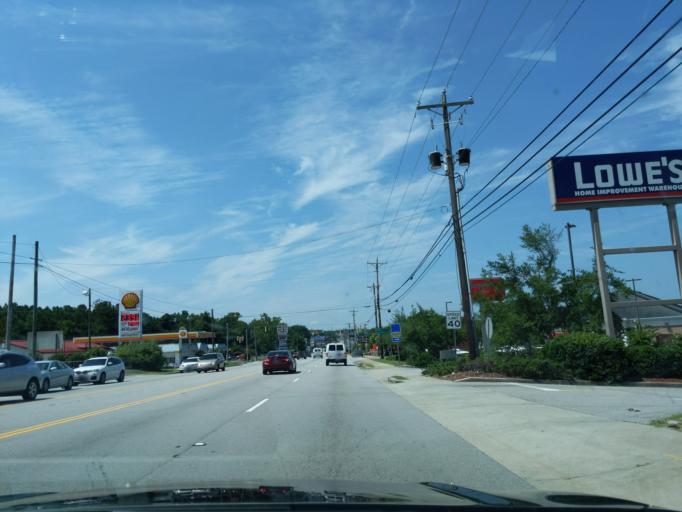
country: US
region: South Carolina
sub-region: Richland County
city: Dentsville
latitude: 34.0713
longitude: -80.9504
